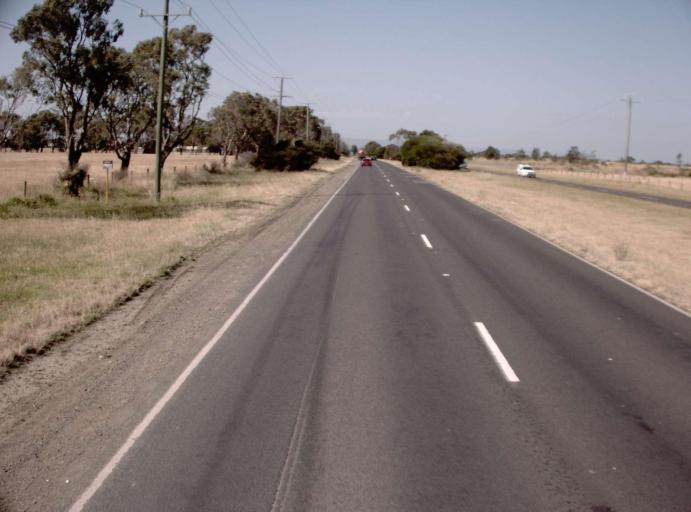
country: AU
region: Victoria
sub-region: Frankston
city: Sandhurst
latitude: -38.0814
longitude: 145.1869
